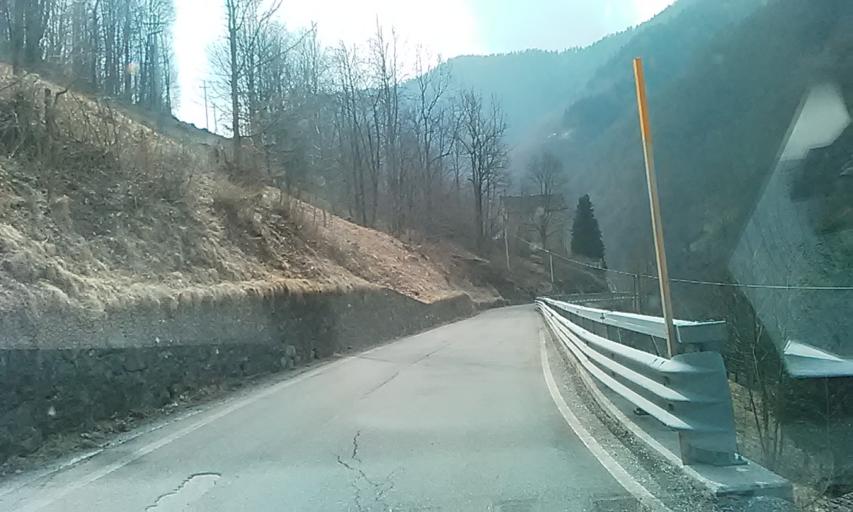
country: IT
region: Piedmont
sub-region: Provincia di Vercelli
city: Fobello
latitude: 45.8984
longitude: 8.1541
